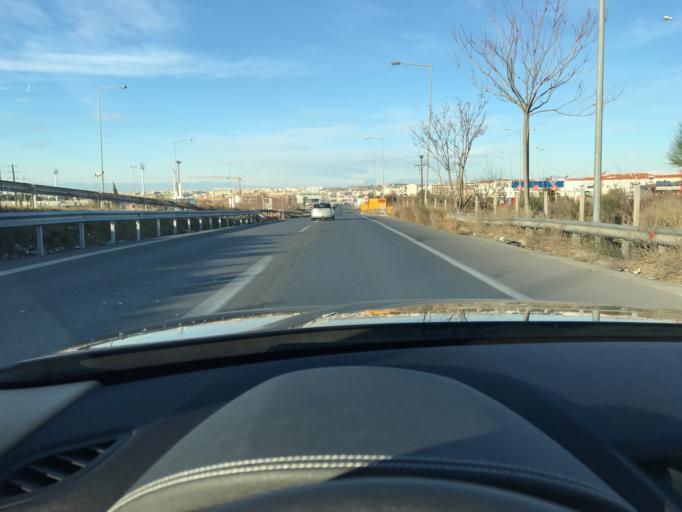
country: GR
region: Central Macedonia
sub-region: Nomos Thessalonikis
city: Efkarpia
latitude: 40.6791
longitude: 22.9573
